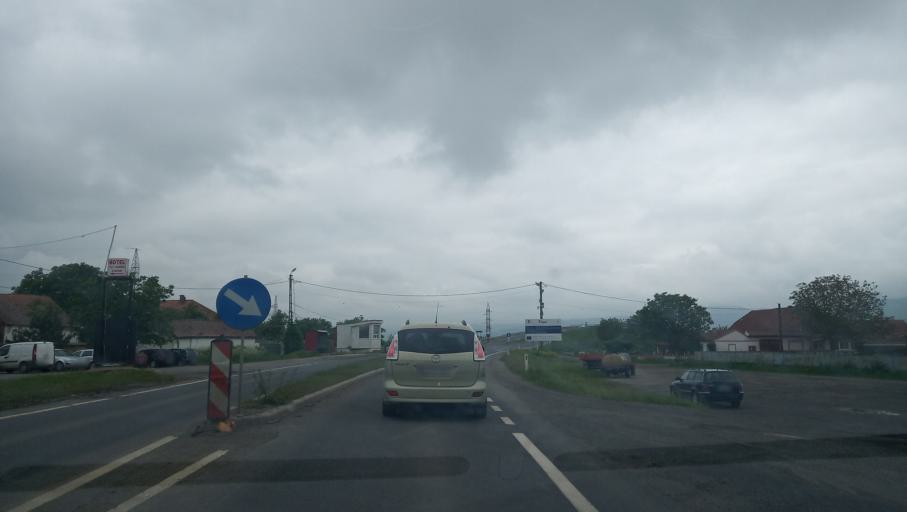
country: RO
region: Alba
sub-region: Comuna Sibot
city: Sibot
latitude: 45.9216
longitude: 23.3447
